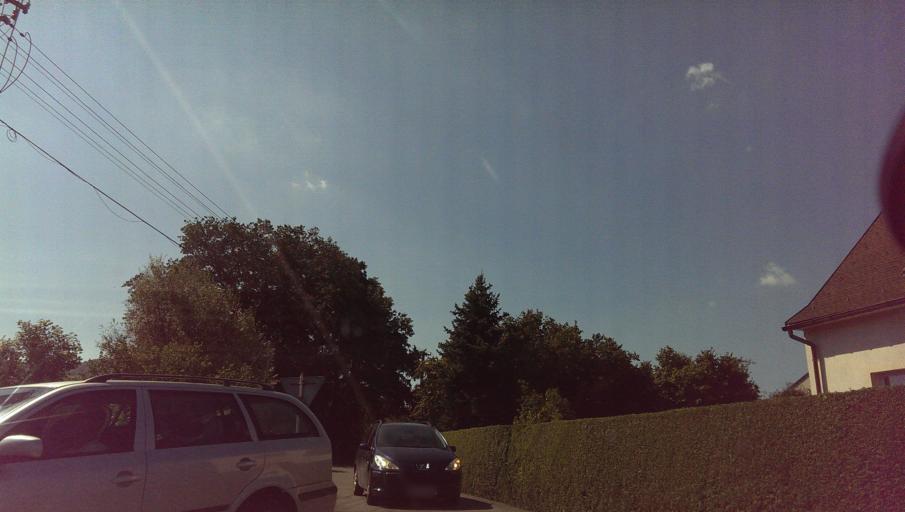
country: CZ
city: Hukvaldy
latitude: 49.6317
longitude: 18.2171
